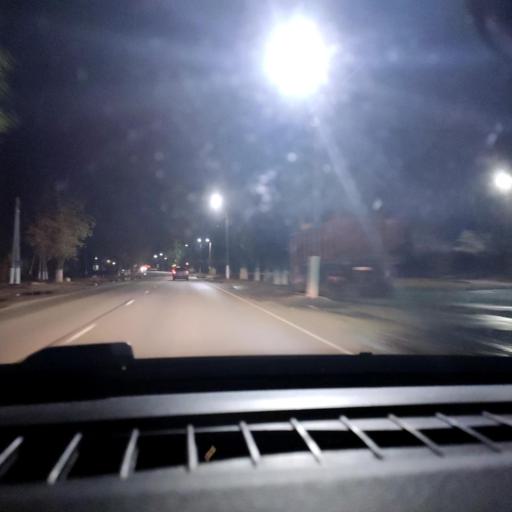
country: RU
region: Voronezj
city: Novaya Usman'
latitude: 51.6352
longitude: 39.4045
